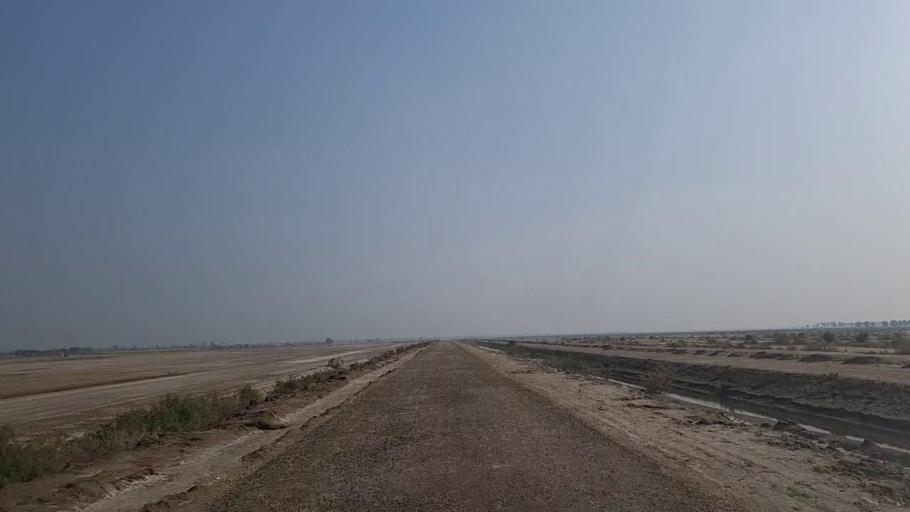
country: PK
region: Sindh
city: Nawabshah
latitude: 26.3462
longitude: 68.4447
